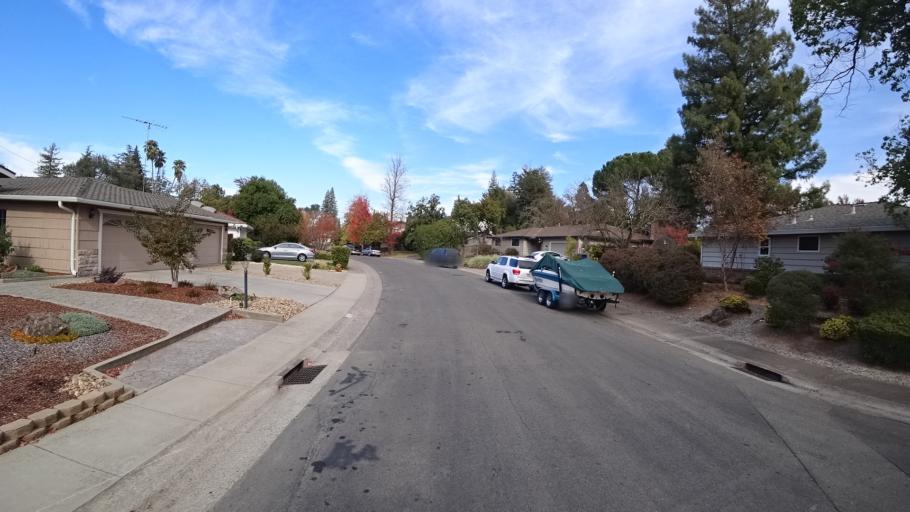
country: US
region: California
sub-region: Sacramento County
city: Fair Oaks
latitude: 38.6690
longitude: -121.2801
